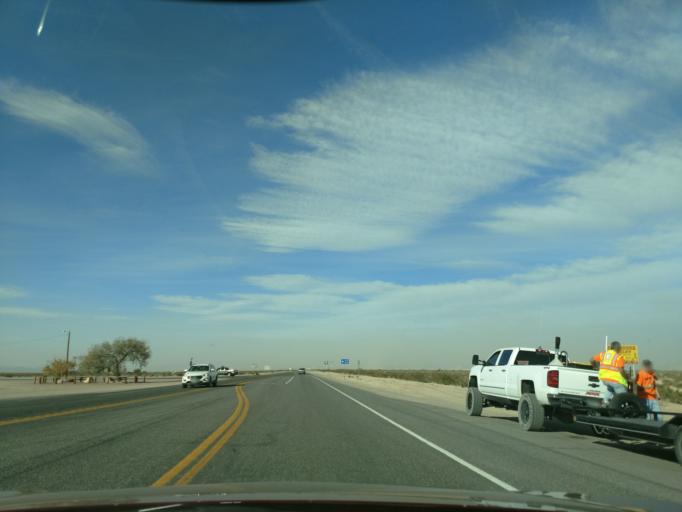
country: US
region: Nevada
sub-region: Nye County
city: Beatty
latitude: 36.6435
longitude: -116.3989
